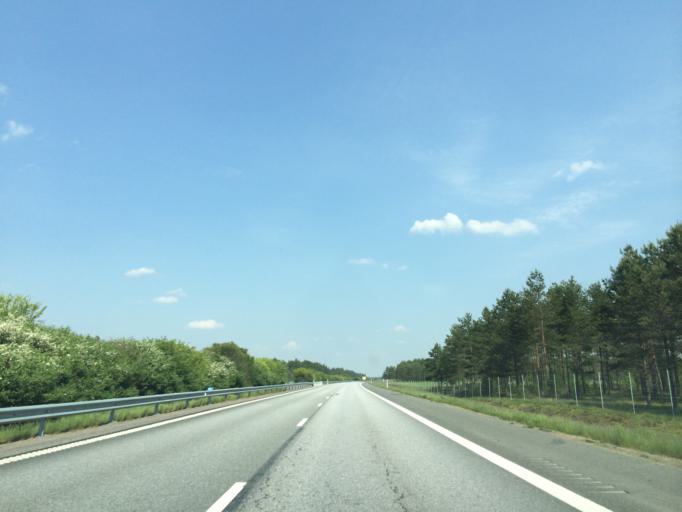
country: SE
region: Joenkoeping
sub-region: Varnamo Kommun
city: Varnamo
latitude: 57.2864
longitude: 14.0844
